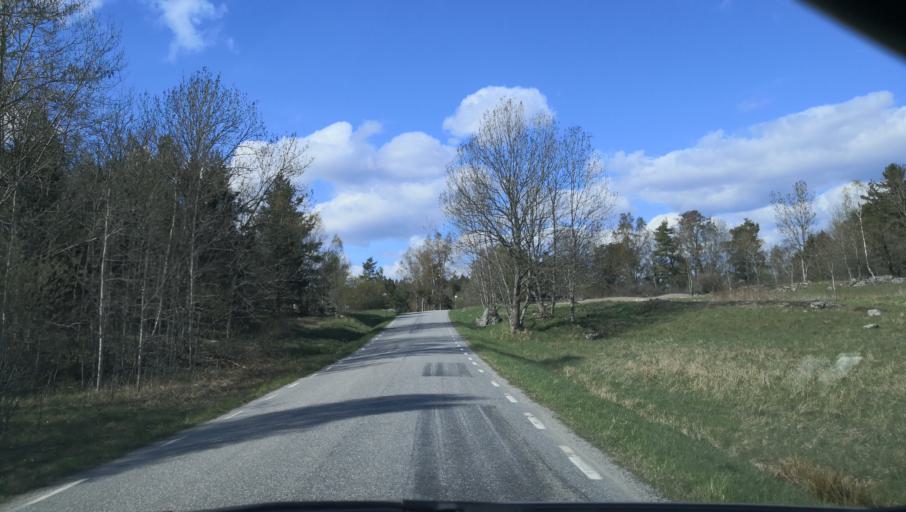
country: SE
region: Stockholm
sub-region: Varmdo Kommun
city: Hemmesta
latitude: 59.4056
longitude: 18.5054
